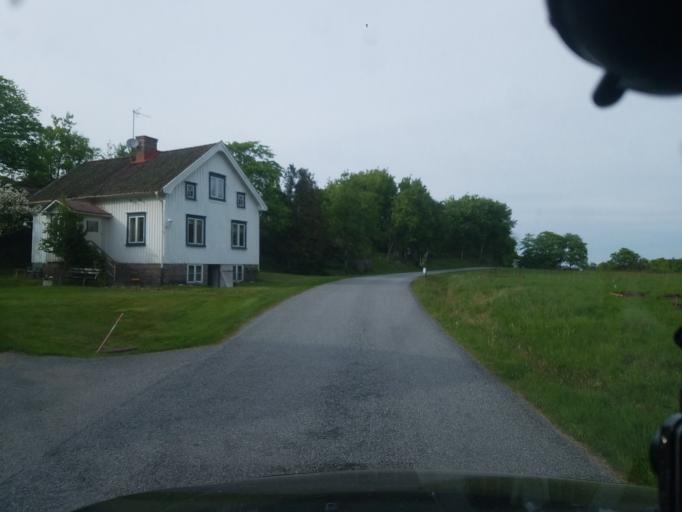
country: SE
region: Vaestra Goetaland
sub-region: Lysekils Kommun
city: Lysekil
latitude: 58.3007
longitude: 11.4509
